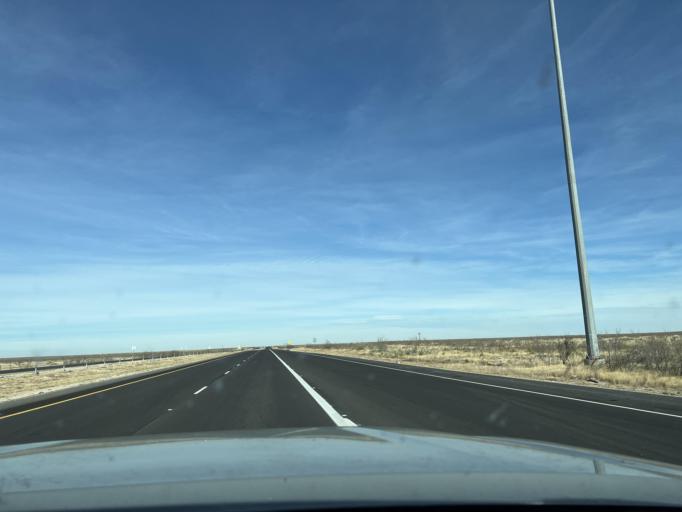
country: US
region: Texas
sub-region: Ector County
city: Gardendale
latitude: 32.0252
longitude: -102.4308
